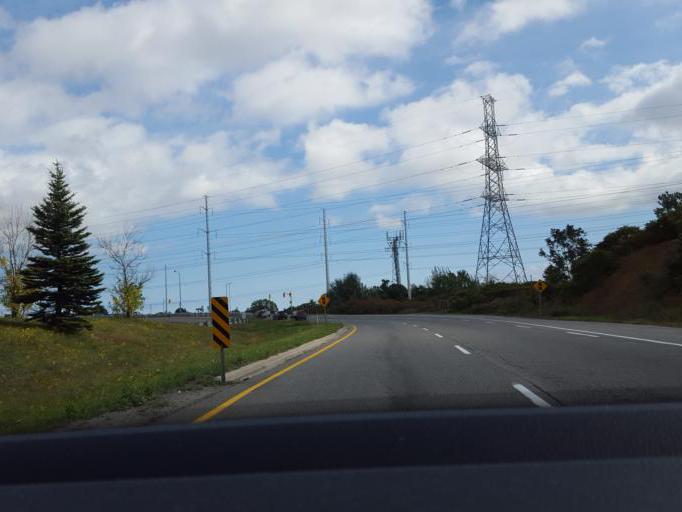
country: CA
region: Ontario
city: Scarborough
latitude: 43.7951
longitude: -79.1989
